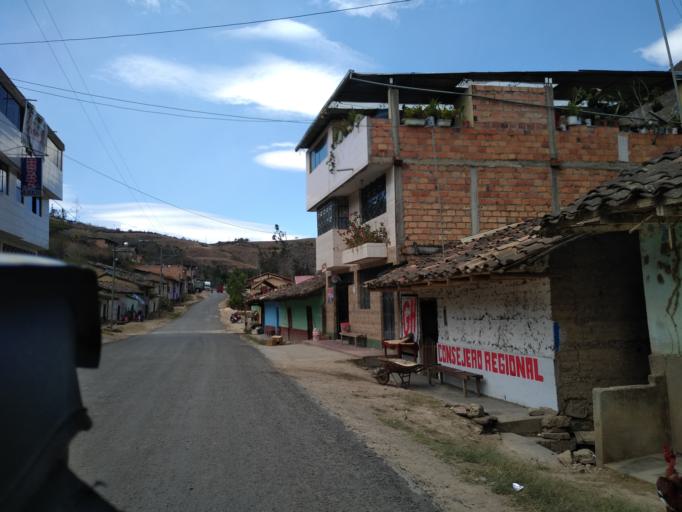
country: PE
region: Amazonas
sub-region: Provincia de Chachapoyas
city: Duraznopampa
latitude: -6.5683
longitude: -77.8283
